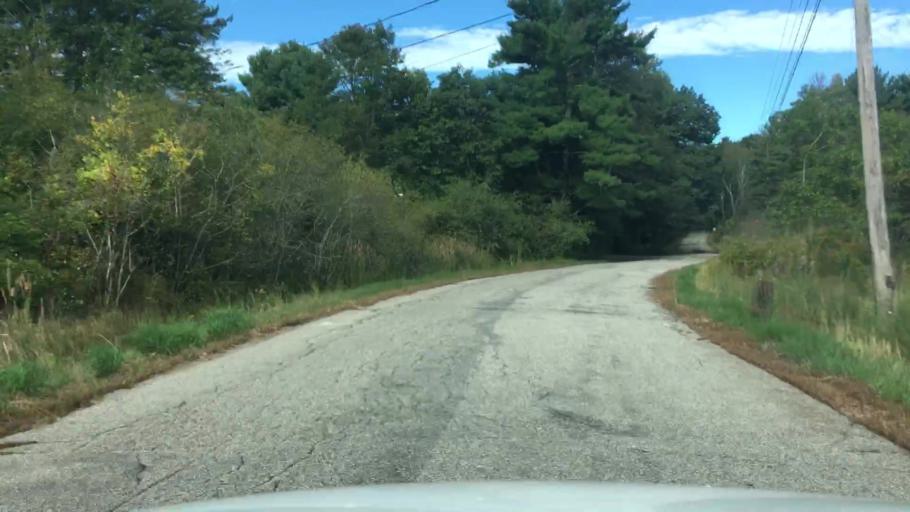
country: US
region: Maine
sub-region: York County
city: York Harbor
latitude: 43.1146
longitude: -70.6715
